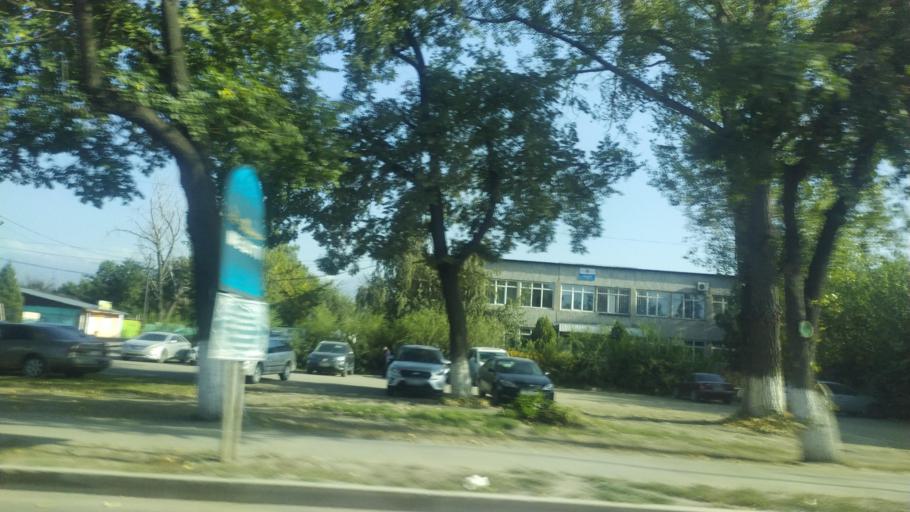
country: KZ
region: Almaty Qalasy
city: Almaty
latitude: 43.2748
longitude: 76.8931
